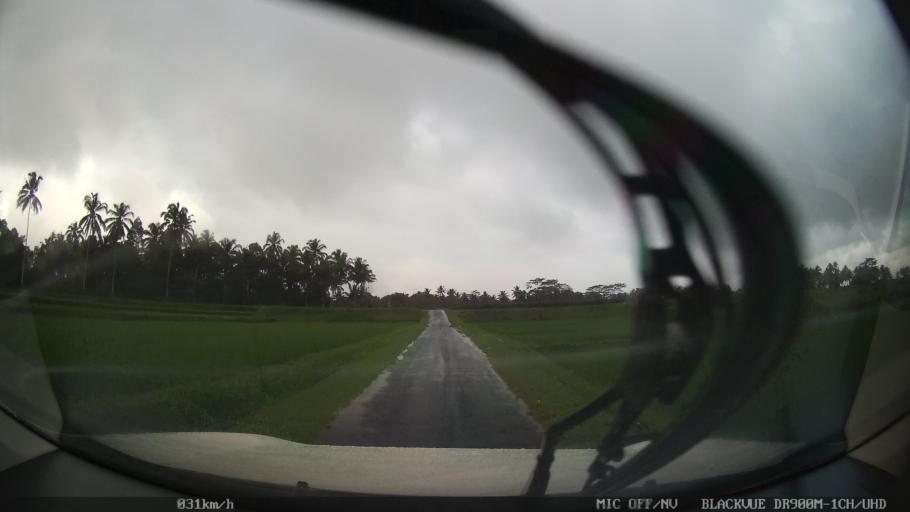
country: ID
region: Bali
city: Kekeran
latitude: -8.4782
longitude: 115.1848
